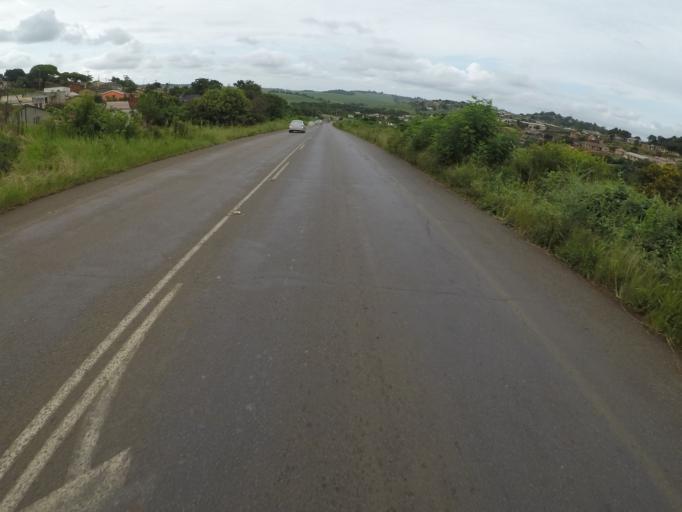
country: ZA
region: KwaZulu-Natal
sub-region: uThungulu District Municipality
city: Empangeni
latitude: -28.7738
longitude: 31.8758
